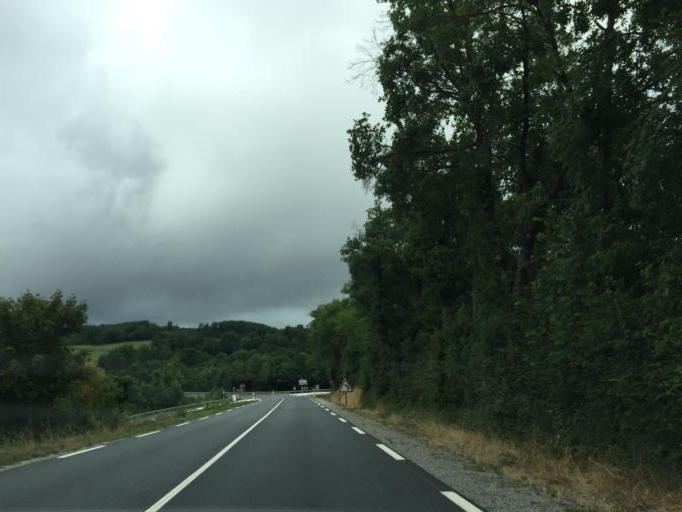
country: FR
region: Midi-Pyrenees
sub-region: Departement de l'Aveyron
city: Severac-le-Chateau
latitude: 44.2357
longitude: 2.9864
